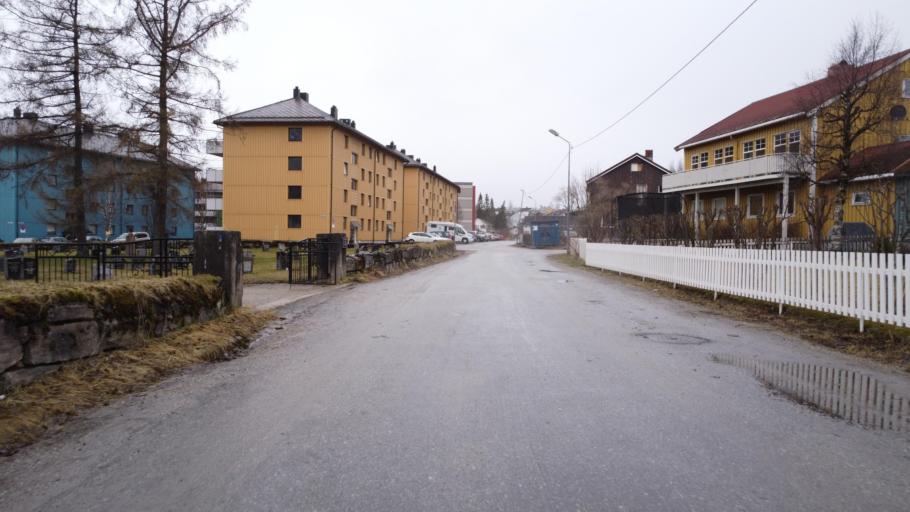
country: NO
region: Nordland
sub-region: Rana
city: Mo i Rana
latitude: 66.3100
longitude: 14.1469
